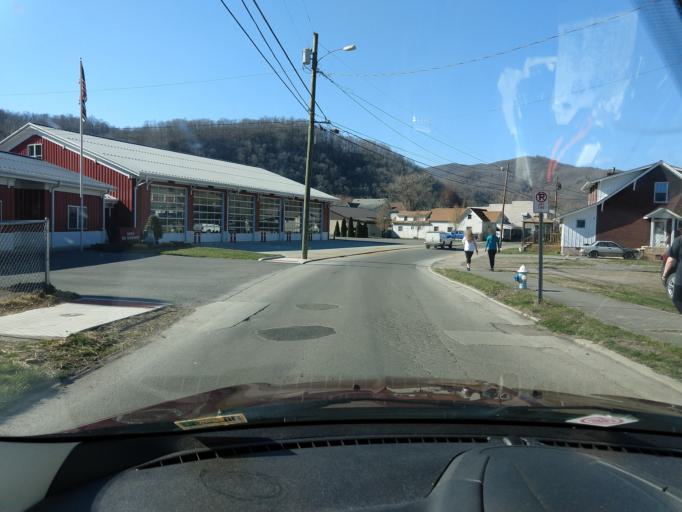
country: US
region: West Virginia
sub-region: Summers County
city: Hinton
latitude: 37.6632
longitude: -80.8937
